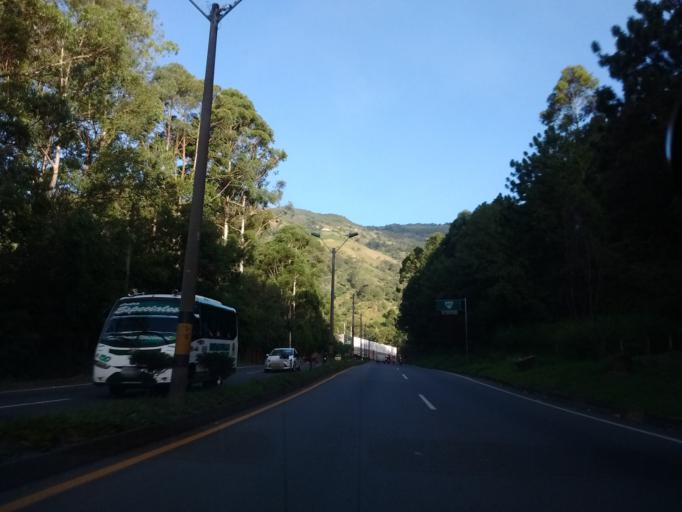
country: CO
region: Antioquia
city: Bello
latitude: 6.3219
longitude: -75.5343
